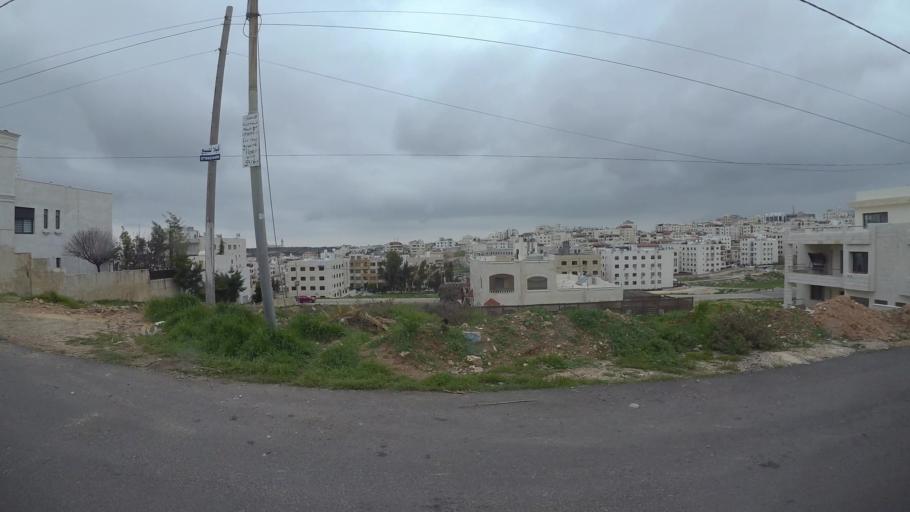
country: JO
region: Amman
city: Al Jubayhah
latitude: 31.9920
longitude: 35.8419
